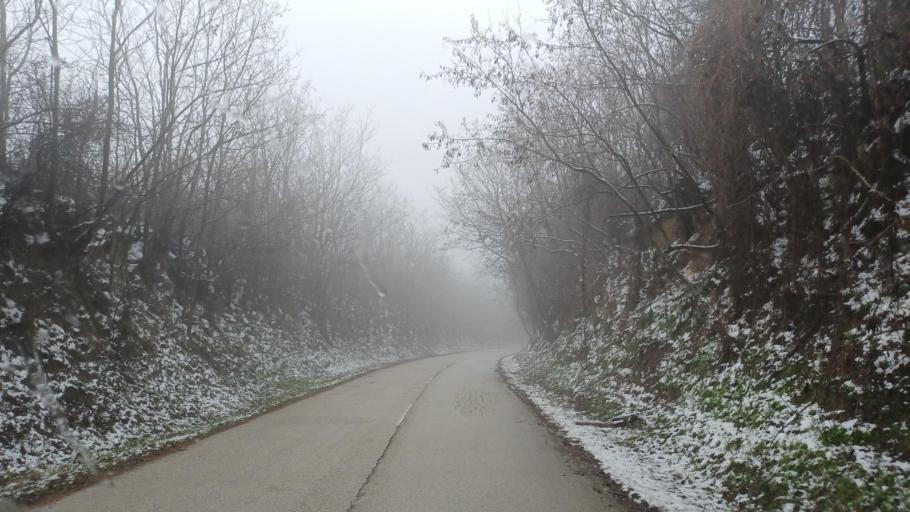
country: HU
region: Tolna
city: Gyonk
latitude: 46.6137
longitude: 18.4820
